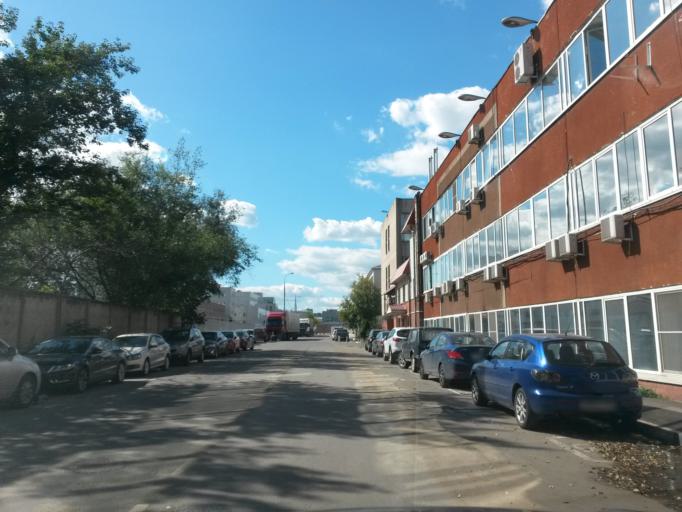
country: RU
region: Moskovskaya
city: Kozhukhovo
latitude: 55.7029
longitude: 37.6988
